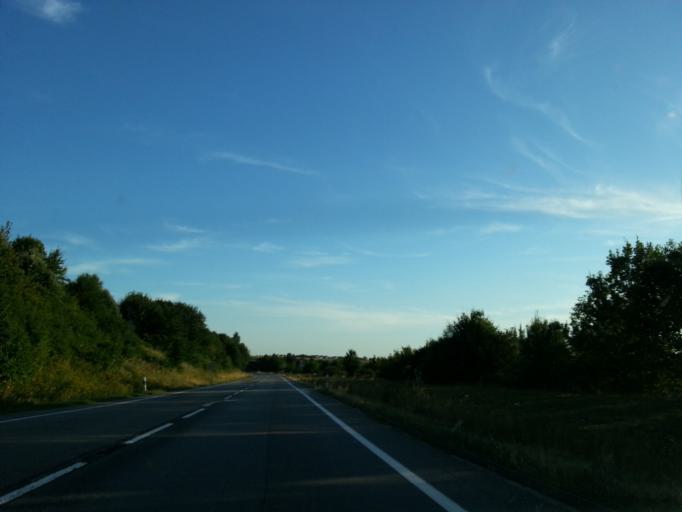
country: DE
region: Rheinland-Pfalz
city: Weselberg
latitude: 49.3443
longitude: 7.6035
